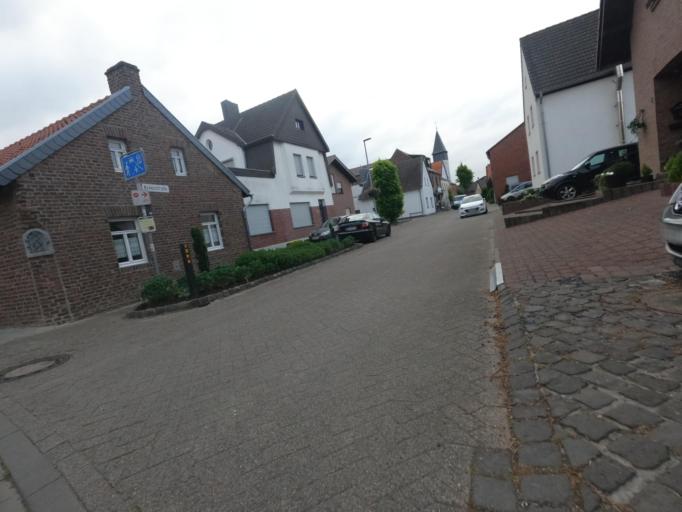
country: NL
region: Limburg
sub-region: Gemeente Roerdalen
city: Vlodrop
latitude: 51.1248
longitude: 6.0993
